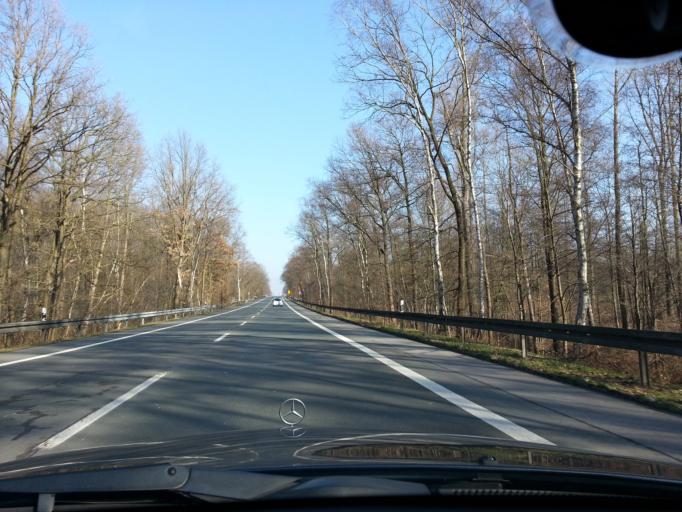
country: DE
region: North Rhine-Westphalia
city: Herten
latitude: 51.5640
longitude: 7.1233
